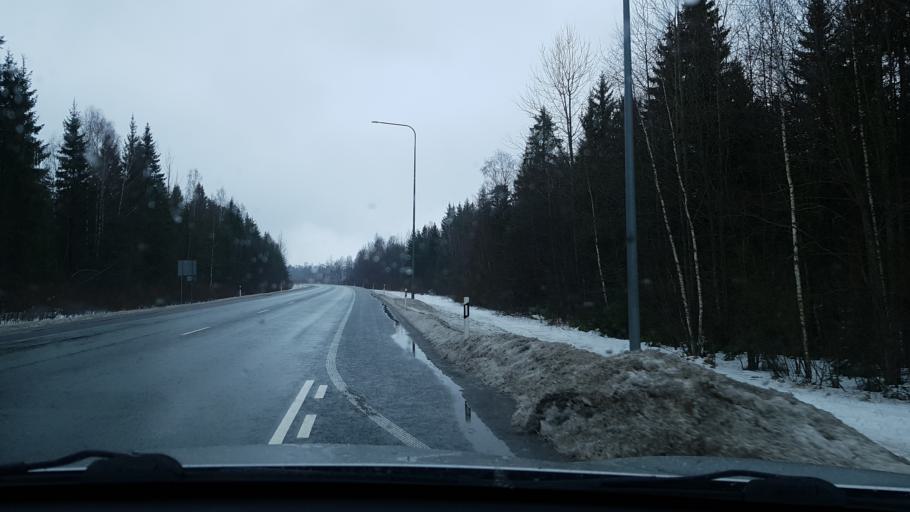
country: EE
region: Raplamaa
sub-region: Kohila vald
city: Kohila
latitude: 59.1307
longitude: 24.7917
